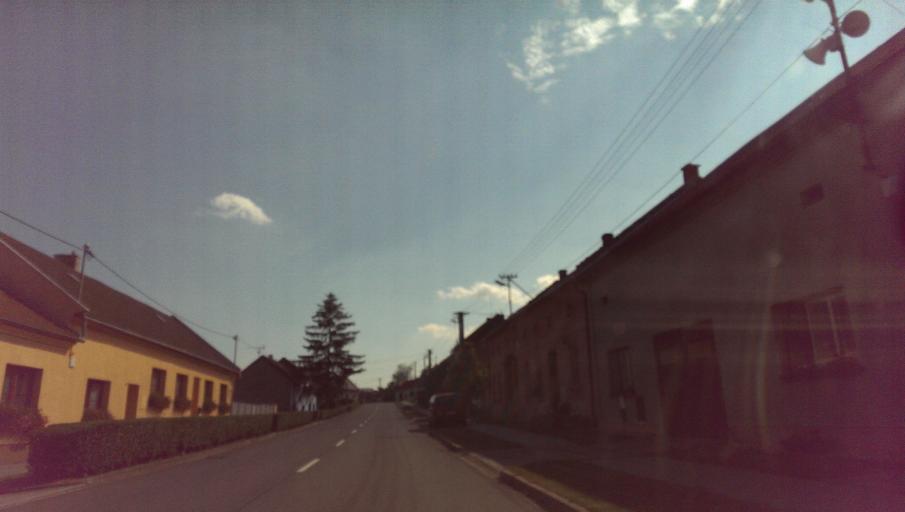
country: CZ
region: Zlin
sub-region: Okres Zlin
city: Otrokovice
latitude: 49.2550
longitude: 17.5431
